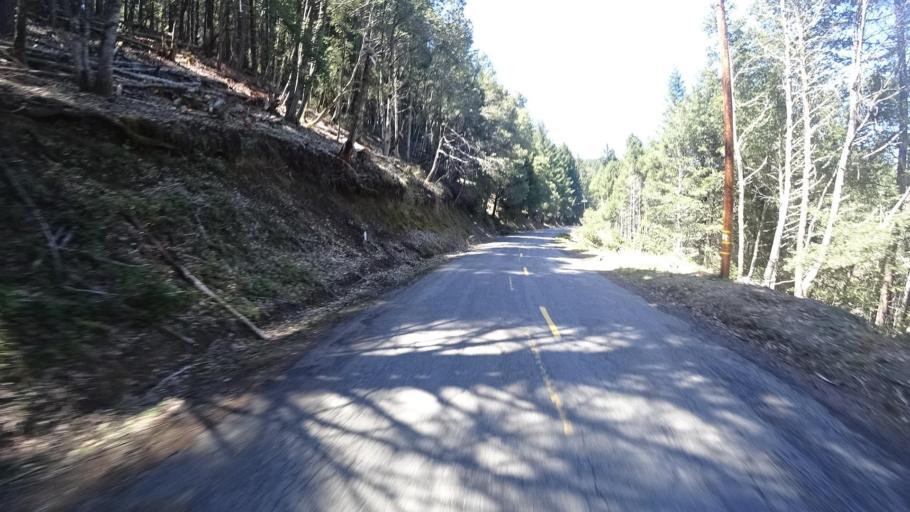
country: US
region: California
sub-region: Humboldt County
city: Rio Dell
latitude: 40.3018
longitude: -124.0599
